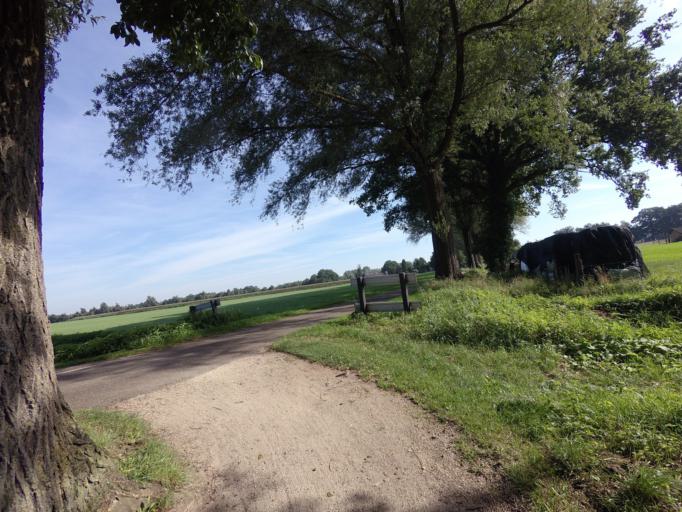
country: NL
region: Gelderland
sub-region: Oost Gelre
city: Lichtenvoorde
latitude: 52.0127
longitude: 6.5185
